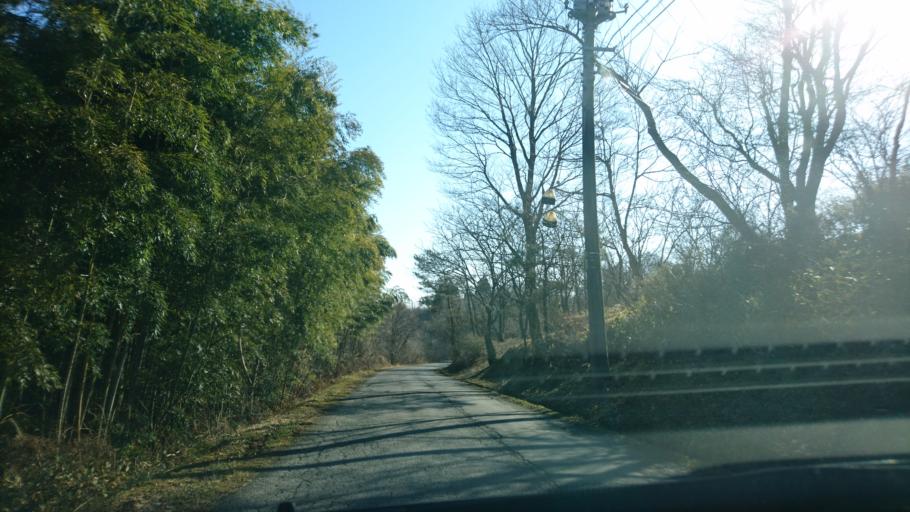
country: JP
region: Iwate
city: Ichinoseki
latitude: 38.8108
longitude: 141.2666
